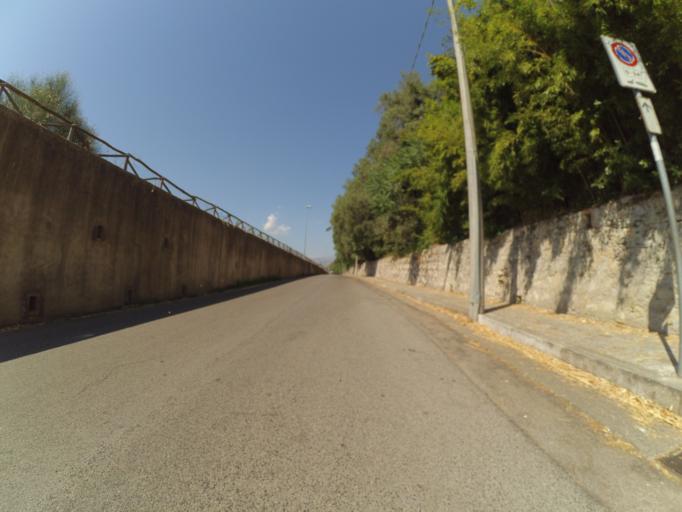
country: IT
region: Latium
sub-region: Provincia di Latina
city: Gaeta
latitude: 41.2070
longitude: 13.5719
